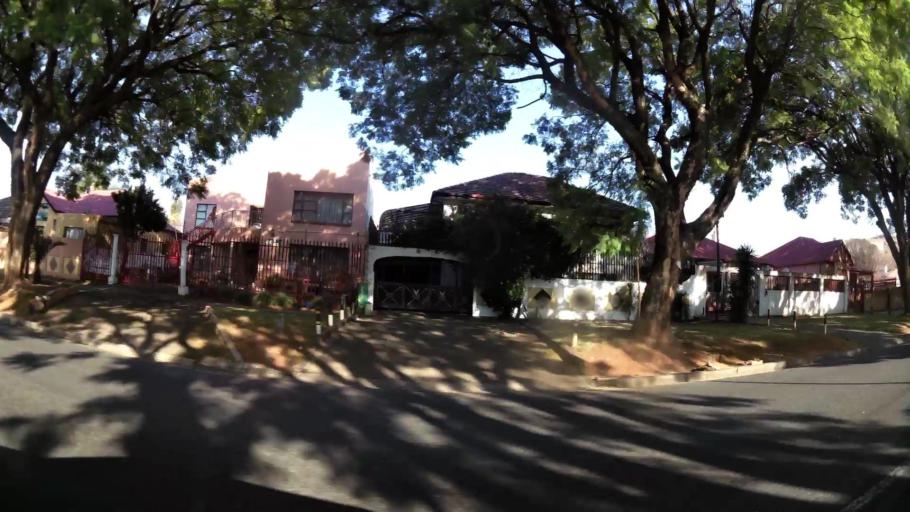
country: ZA
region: Gauteng
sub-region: City of Johannesburg Metropolitan Municipality
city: Johannesburg
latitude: -26.1892
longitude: 28.0910
